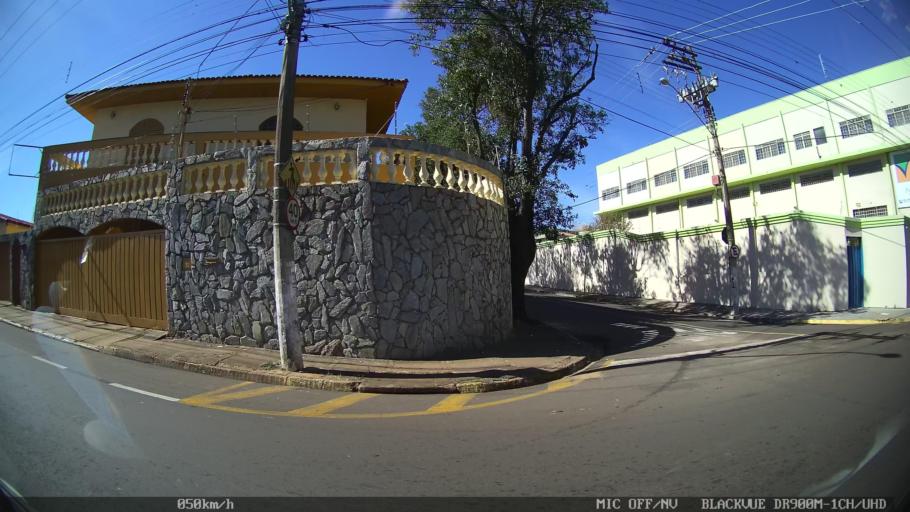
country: BR
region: Sao Paulo
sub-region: Franca
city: Franca
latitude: -20.5221
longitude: -47.3999
